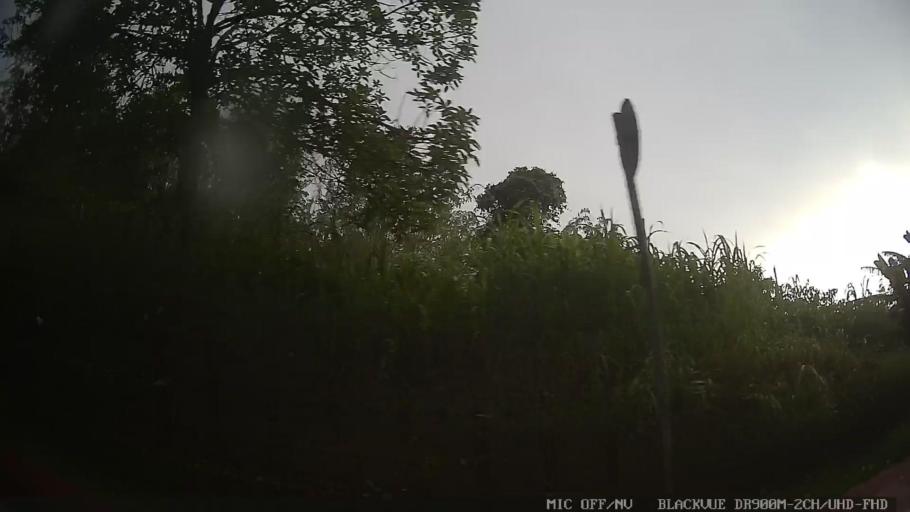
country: BR
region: Sao Paulo
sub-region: Ribeirao Pires
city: Ribeirao Pires
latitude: -23.6999
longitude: -46.3863
